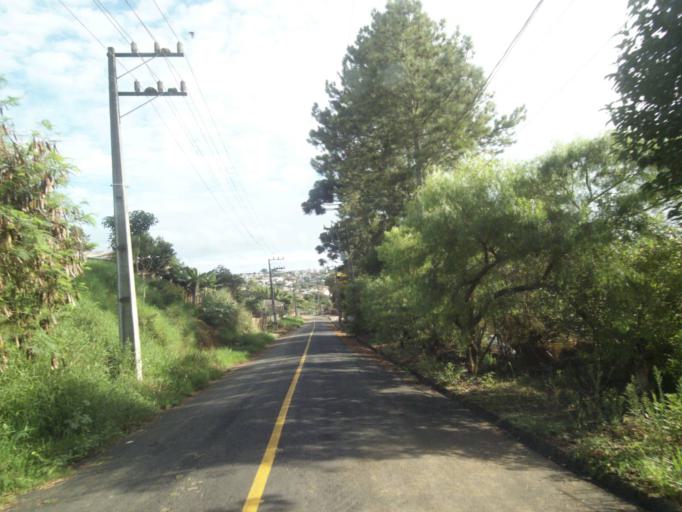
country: BR
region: Parana
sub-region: Telemaco Borba
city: Telemaco Borba
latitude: -24.3428
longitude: -50.6177
